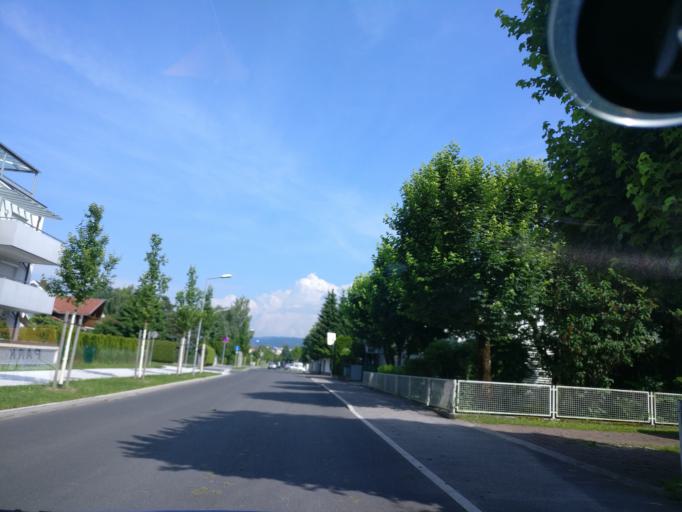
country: AT
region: Carinthia
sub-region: Klagenfurt am Woerthersee
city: Klagenfurt am Woerthersee
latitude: 46.6135
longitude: 14.2709
